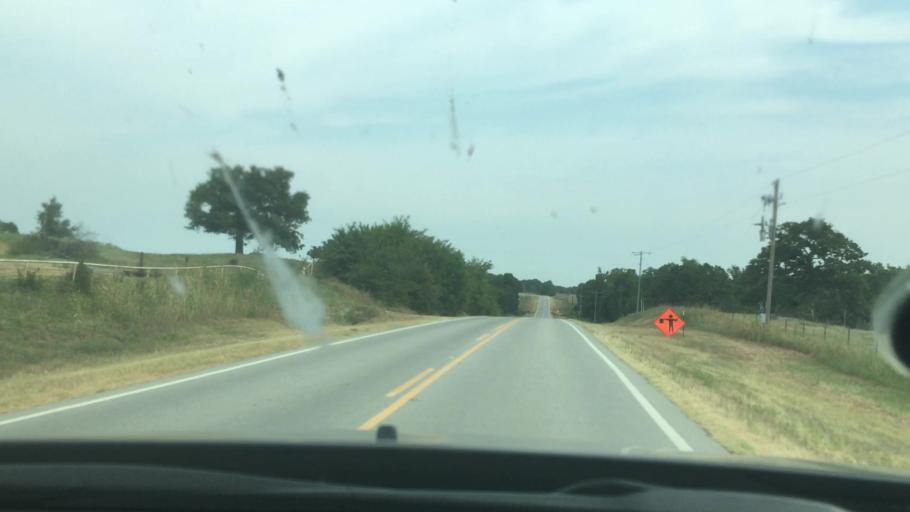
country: US
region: Oklahoma
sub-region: Coal County
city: Coalgate
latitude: 34.5693
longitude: -96.4069
